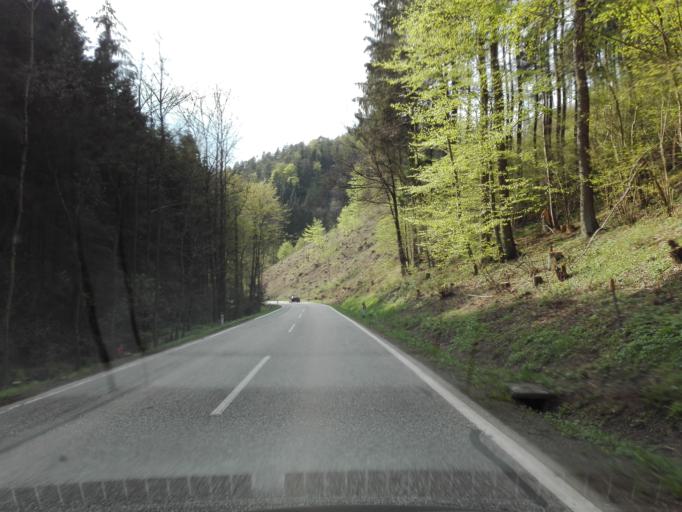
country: AT
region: Upper Austria
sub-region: Politischer Bezirk Urfahr-Umgebung
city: Feldkirchen an der Donau
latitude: 48.3834
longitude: 14.0731
